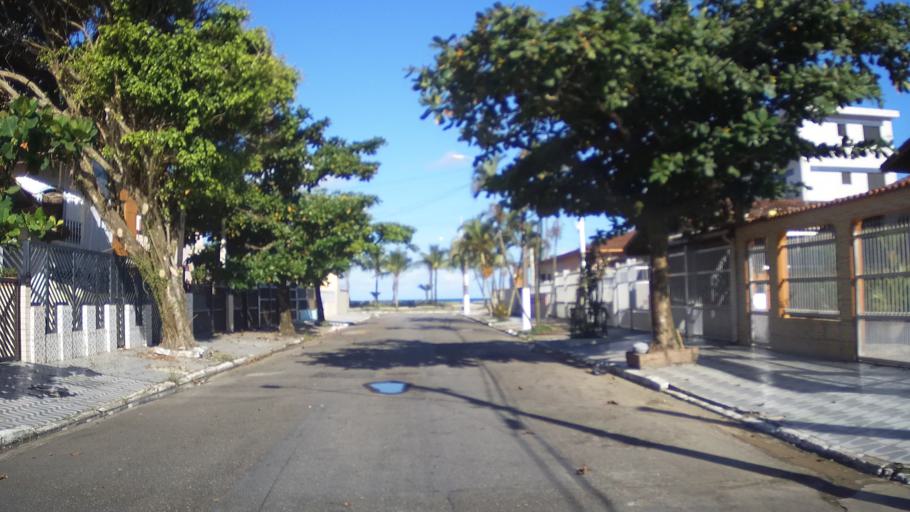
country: BR
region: Sao Paulo
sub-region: Mongagua
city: Mongagua
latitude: -24.0604
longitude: -46.5476
